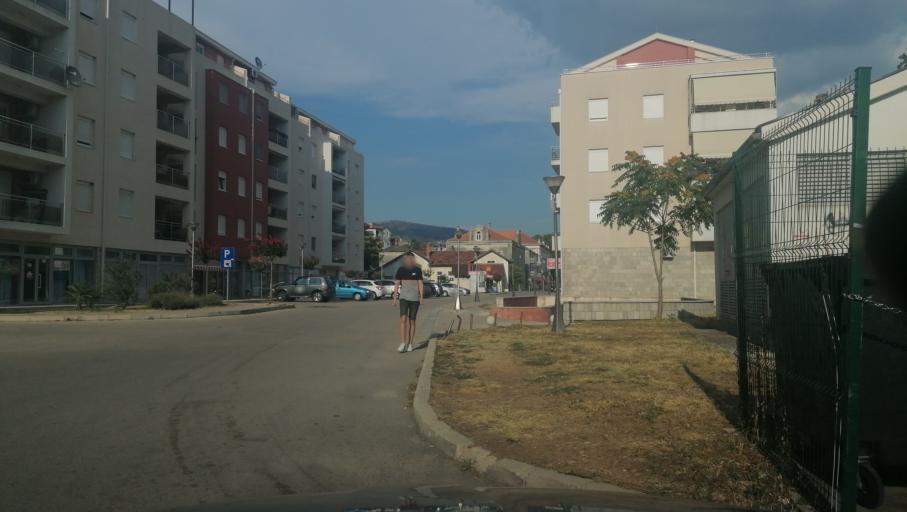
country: BA
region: Republika Srpska
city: Trebinje
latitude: 42.7110
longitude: 18.3409
